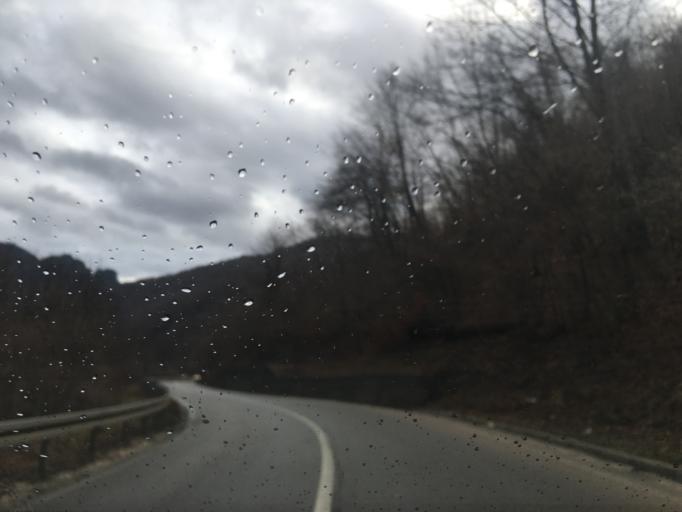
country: RS
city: Sokolovo Brdo
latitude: 43.2018
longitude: 19.7620
